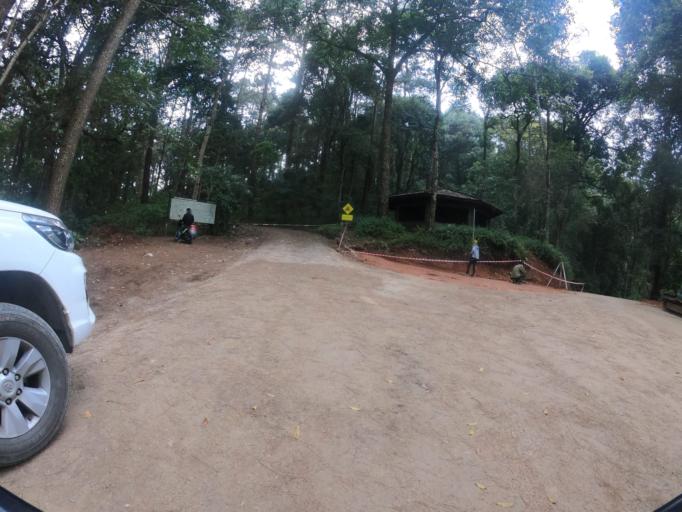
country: TH
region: Chiang Mai
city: Chiang Mai
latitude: 18.8231
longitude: 98.8900
